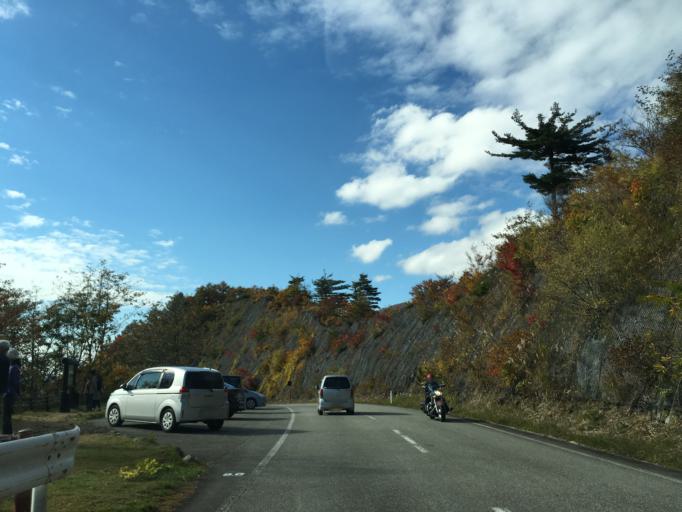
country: JP
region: Fukushima
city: Inawashiro
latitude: 37.6761
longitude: 140.1250
